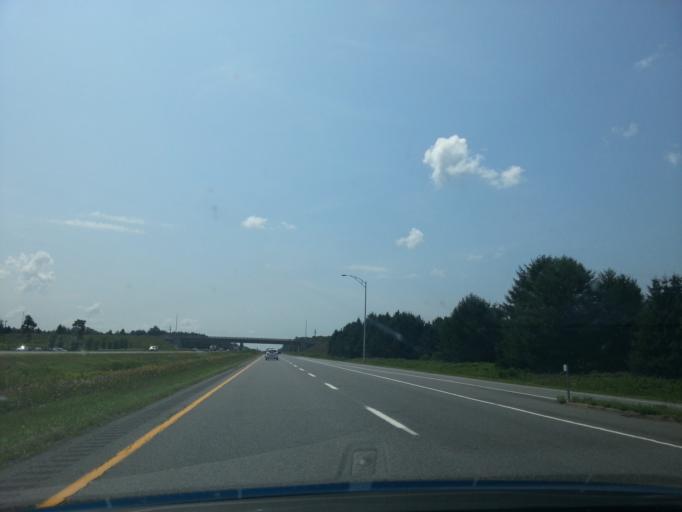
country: CA
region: Quebec
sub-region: Mauricie
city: Princeville
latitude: 46.3195
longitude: -71.9361
